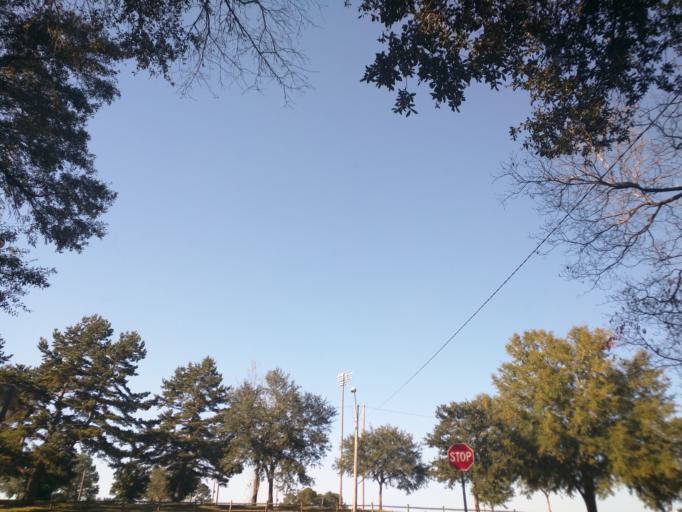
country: US
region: Florida
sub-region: Leon County
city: Tallahassee
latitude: 30.4430
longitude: -84.2175
